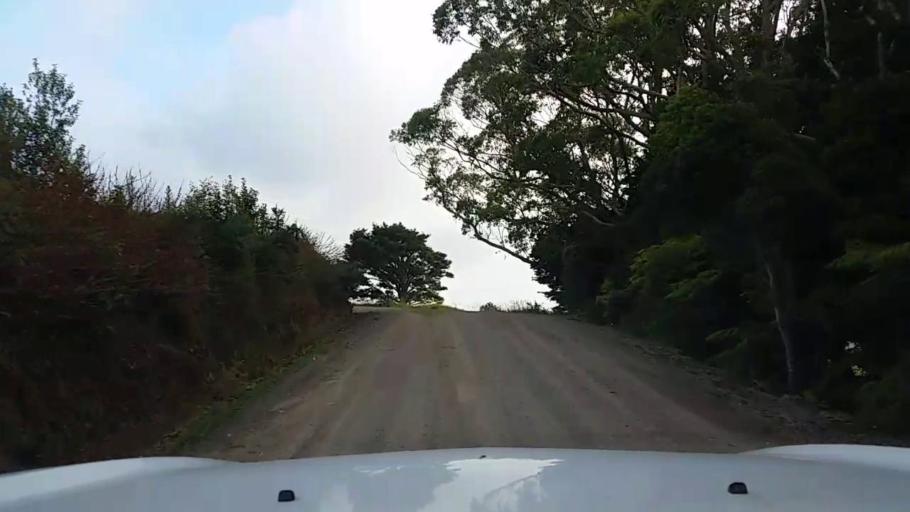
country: NZ
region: Northland
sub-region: Whangarei
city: Maungatapere
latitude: -35.6697
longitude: 174.1755
